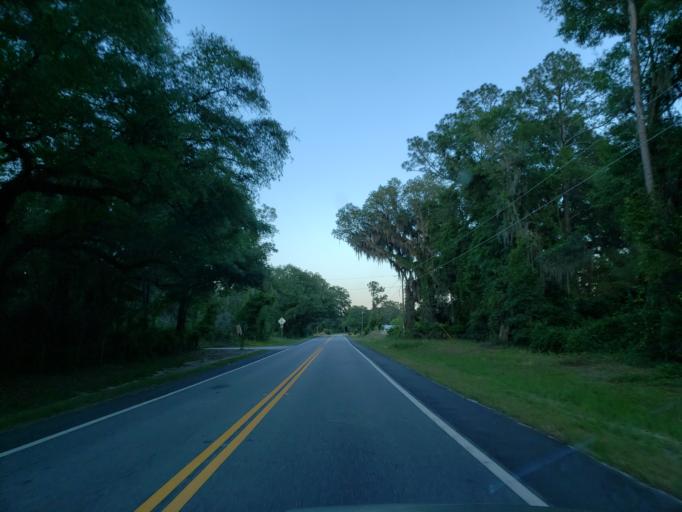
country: US
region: Georgia
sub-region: Echols County
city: Statenville
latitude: 30.5585
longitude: -83.1332
